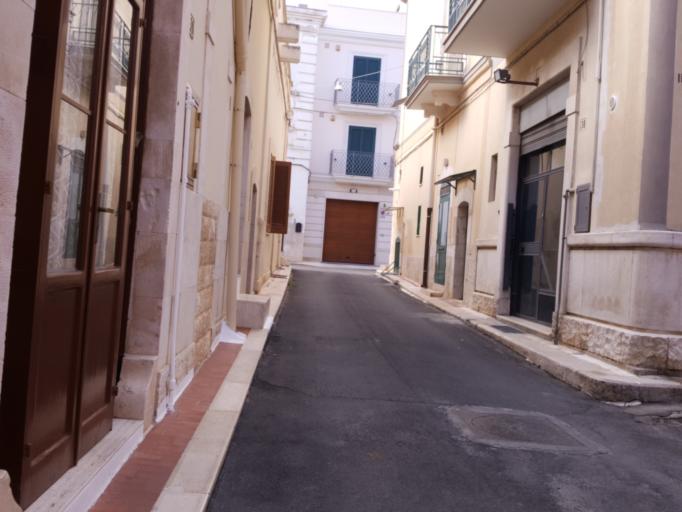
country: IT
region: Apulia
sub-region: Provincia di Bari
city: Triggiano
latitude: 41.0629
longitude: 16.9240
